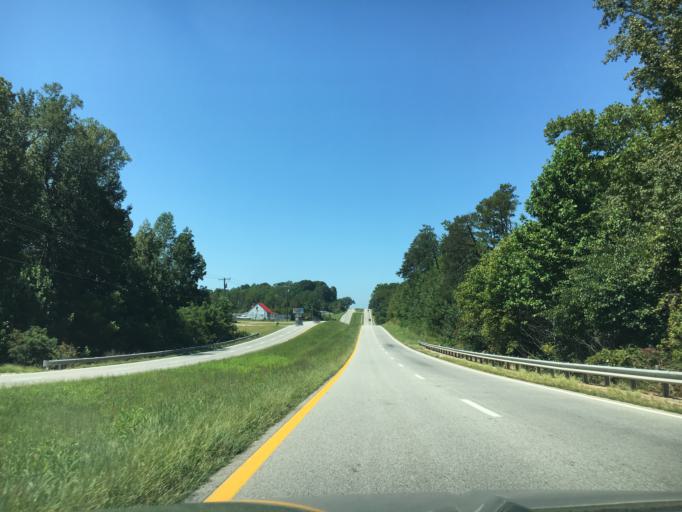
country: US
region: Virginia
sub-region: City of Danville
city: Danville
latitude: 36.5808
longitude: -79.2675
